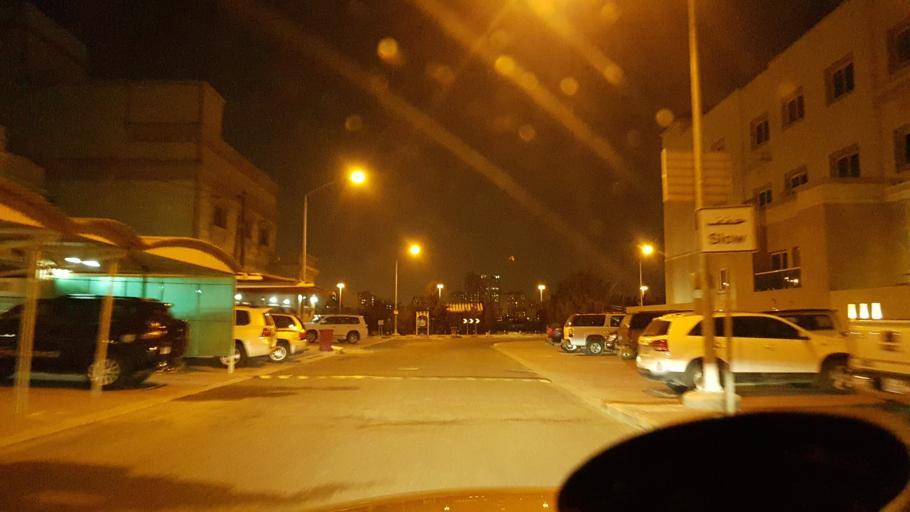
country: KW
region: Al Ahmadi
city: Al Manqaf
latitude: 29.1171
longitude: 48.1267
